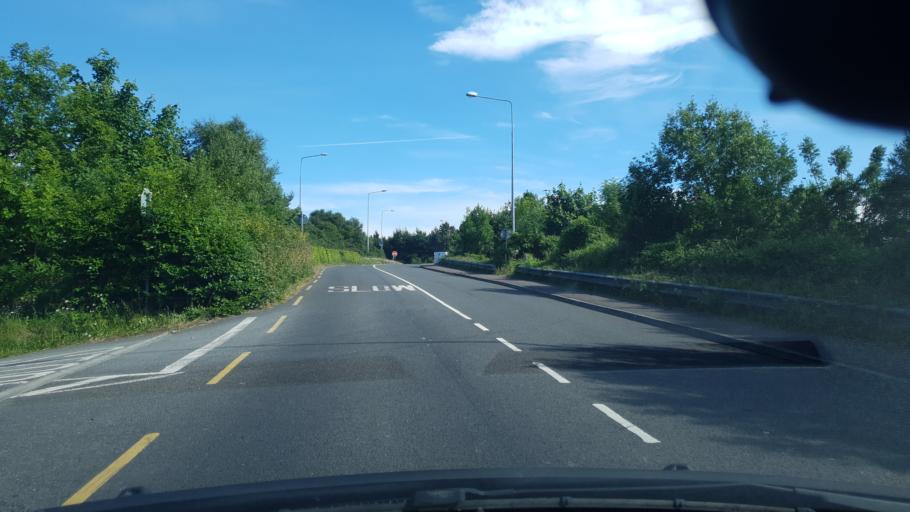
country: IE
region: Munster
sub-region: Ciarrai
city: Cill Airne
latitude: 52.0704
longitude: -9.5057
